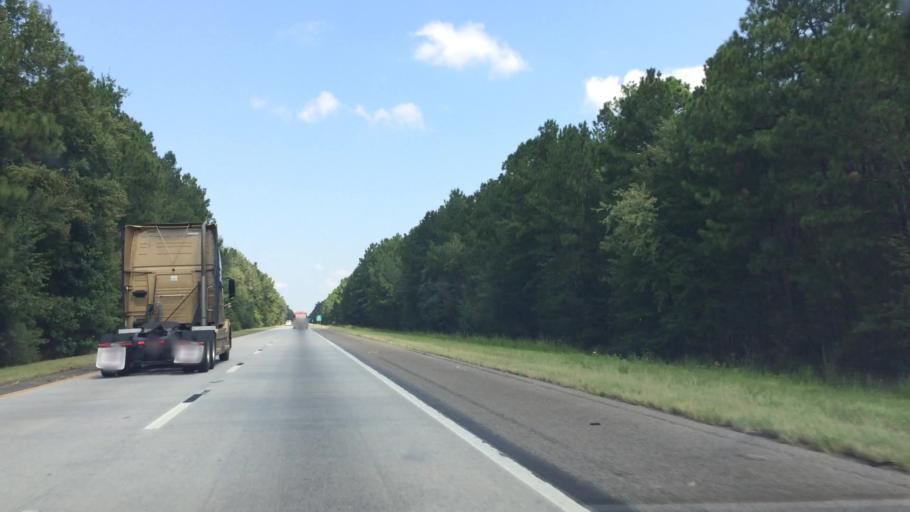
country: US
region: South Carolina
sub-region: Dorchester County
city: Saint George
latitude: 33.0621
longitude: -80.6625
